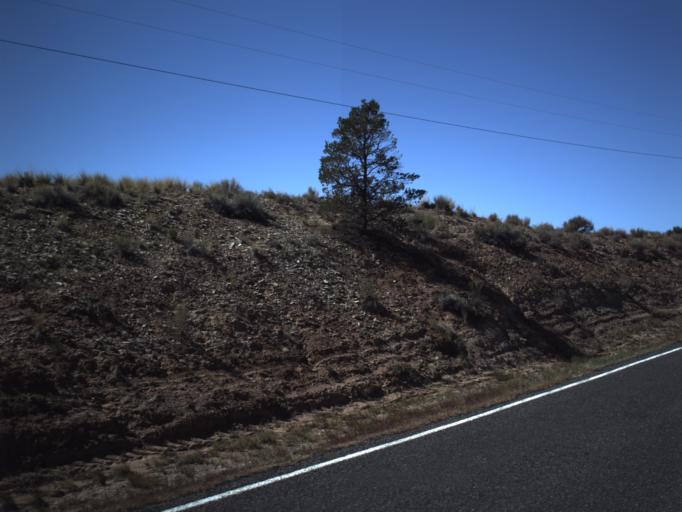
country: US
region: Utah
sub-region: Wayne County
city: Loa
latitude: 37.7415
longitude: -111.5563
